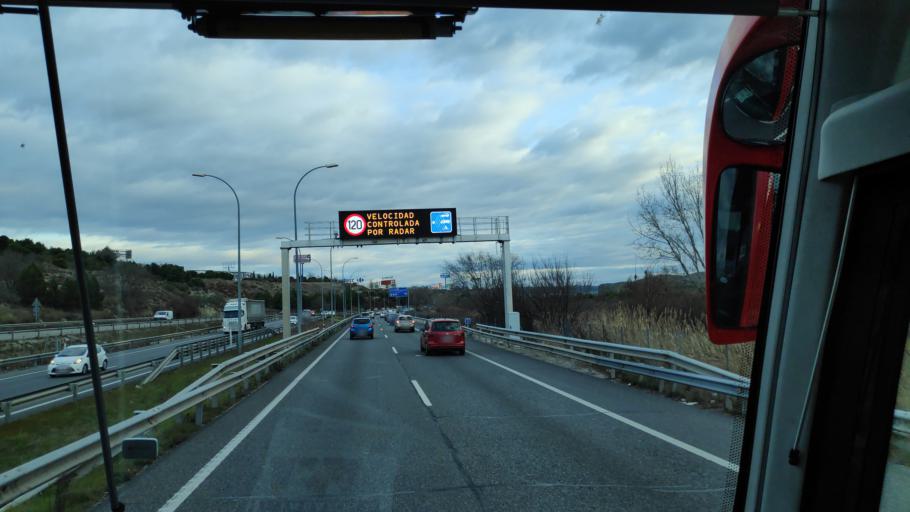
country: ES
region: Madrid
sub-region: Provincia de Madrid
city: Vaciamadrid
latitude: 40.3462
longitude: -3.5435
